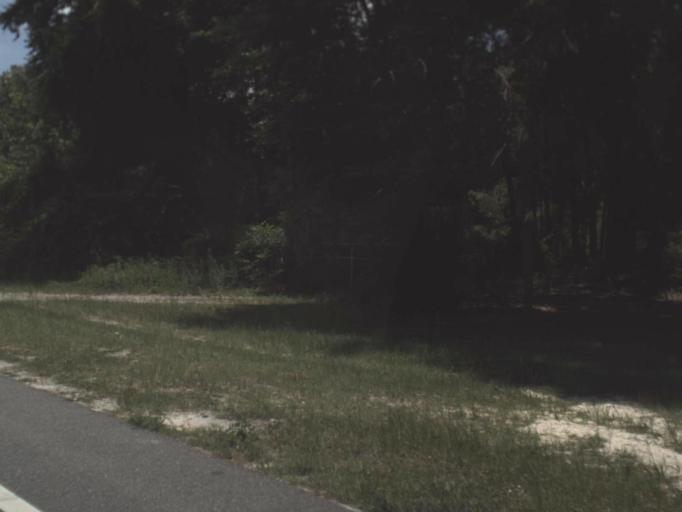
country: US
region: Florida
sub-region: Dixie County
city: Cross City
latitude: 29.6922
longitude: -82.9843
